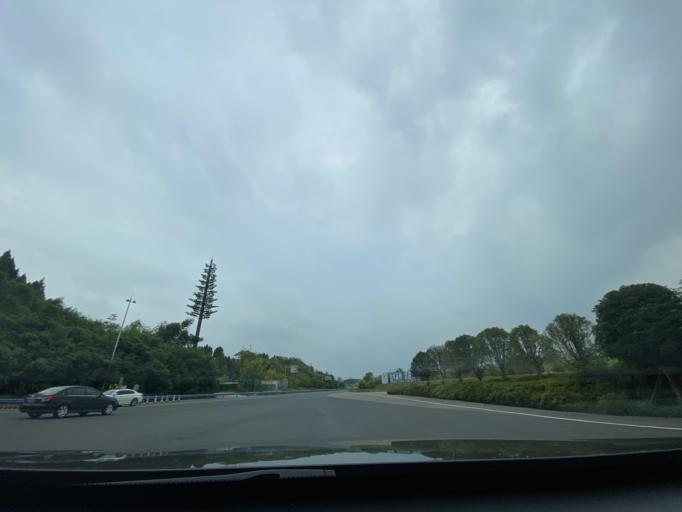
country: CN
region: Sichuan
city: Jiancheng
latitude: 30.4985
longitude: 104.4479
